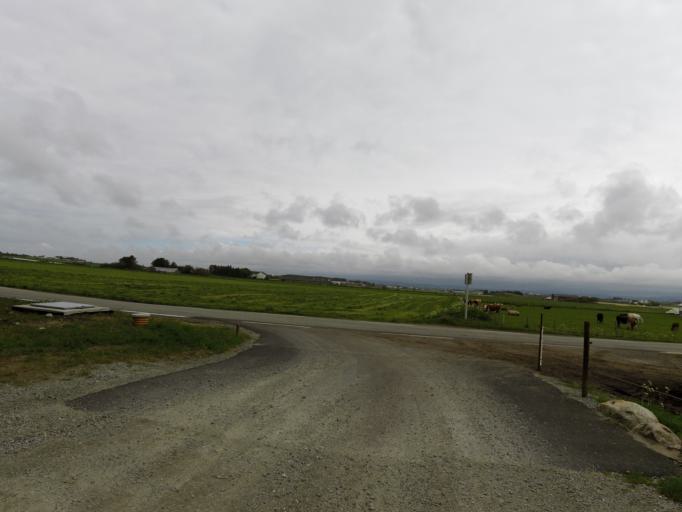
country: NO
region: Rogaland
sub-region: Ha
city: Naerbo
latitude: 58.6942
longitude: 5.5543
